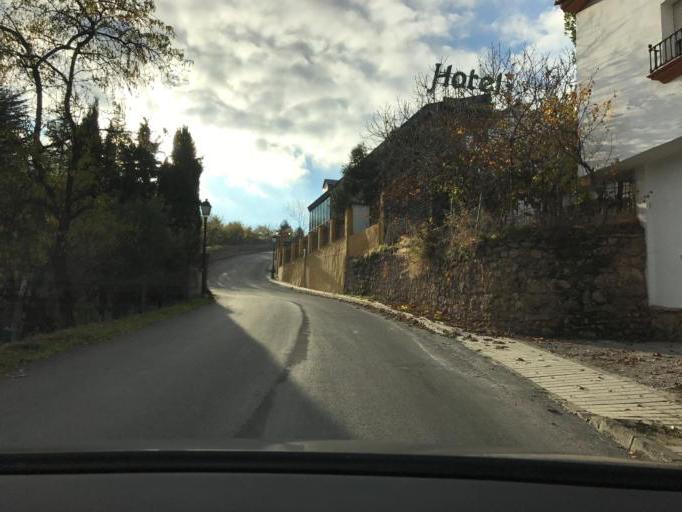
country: ES
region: Andalusia
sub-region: Provincia de Granada
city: Monachil
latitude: 37.1198
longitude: -3.5447
